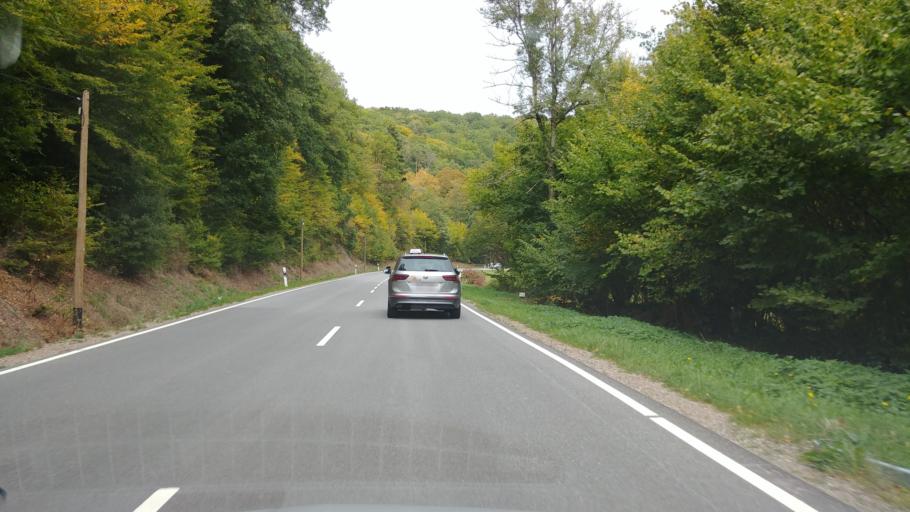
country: DE
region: Rheinland-Pfalz
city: Eisighofen
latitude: 50.2252
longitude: 8.0398
